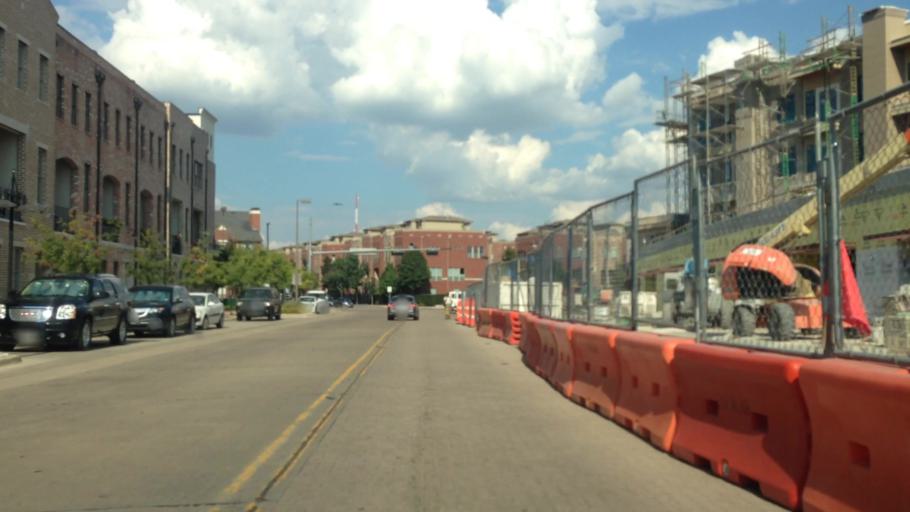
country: US
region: Texas
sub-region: Dallas County
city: Dallas
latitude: 32.7783
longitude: -96.7897
